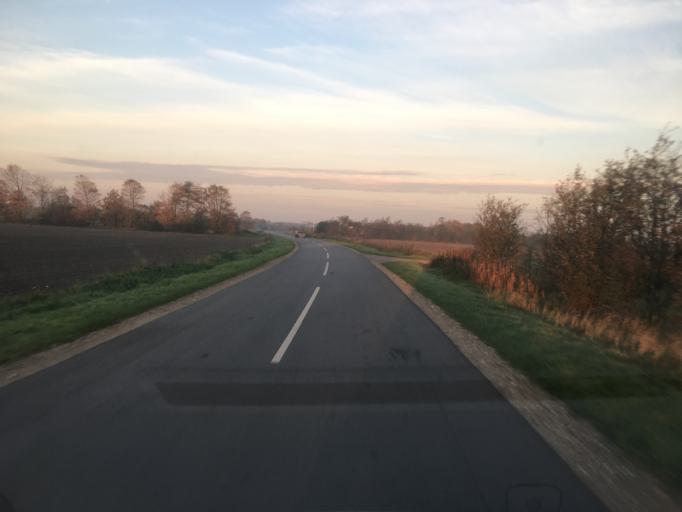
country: DK
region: South Denmark
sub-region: Tonder Kommune
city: Logumkloster
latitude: 55.0610
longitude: 8.9777
